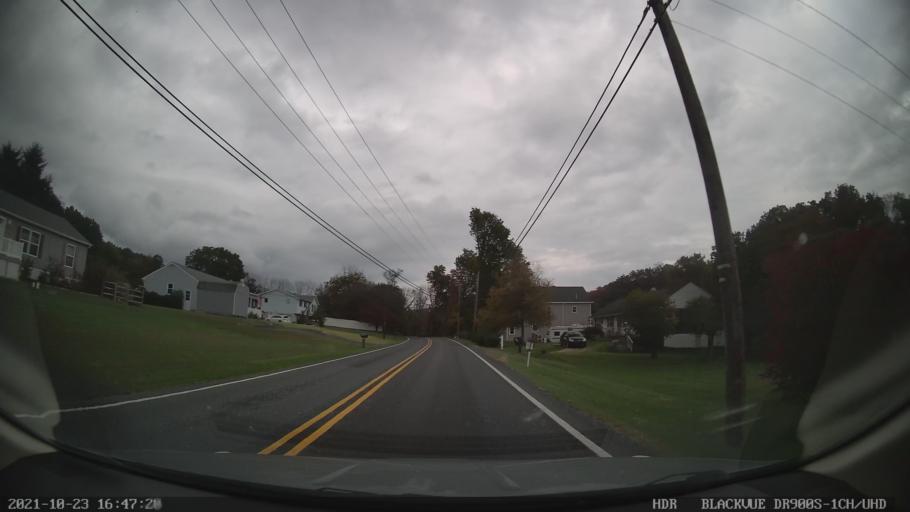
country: US
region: Pennsylvania
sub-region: Berks County
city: Red Lion
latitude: 40.4895
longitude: -75.6392
